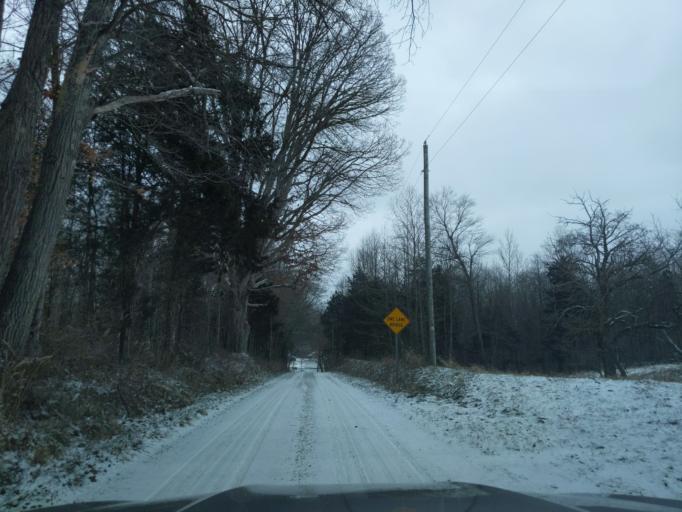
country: US
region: Indiana
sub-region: Decatur County
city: Westport
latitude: 39.2042
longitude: -85.4486
